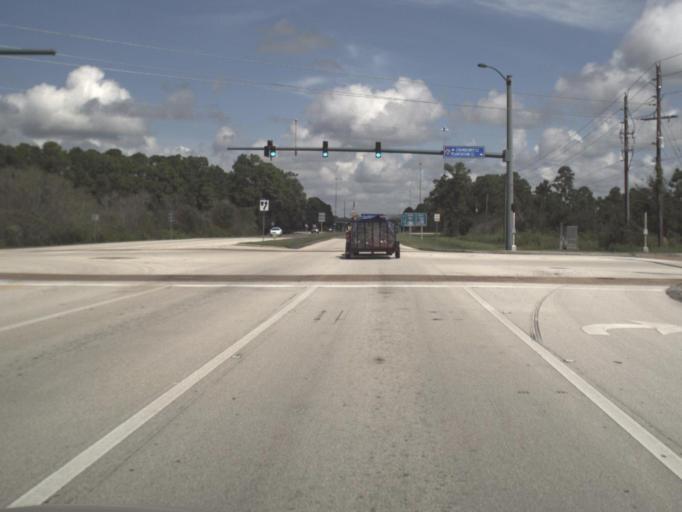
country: US
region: Florida
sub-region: Sarasota County
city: North Port
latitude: 27.0935
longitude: -82.1554
